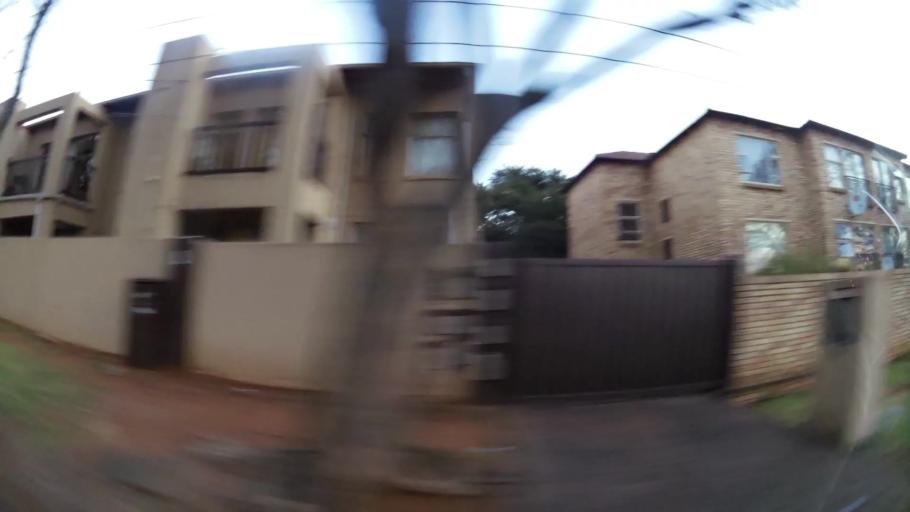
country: ZA
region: Gauteng
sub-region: City of Johannesburg Metropolitan Municipality
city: Roodepoort
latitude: -26.1693
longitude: 27.9076
